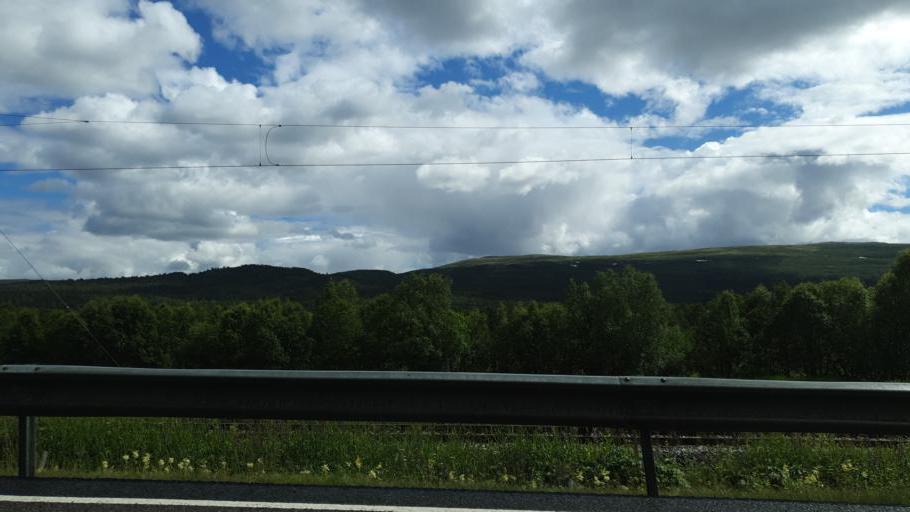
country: NO
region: Sor-Trondelag
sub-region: Oppdal
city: Oppdal
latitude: 62.6148
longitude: 9.7539
